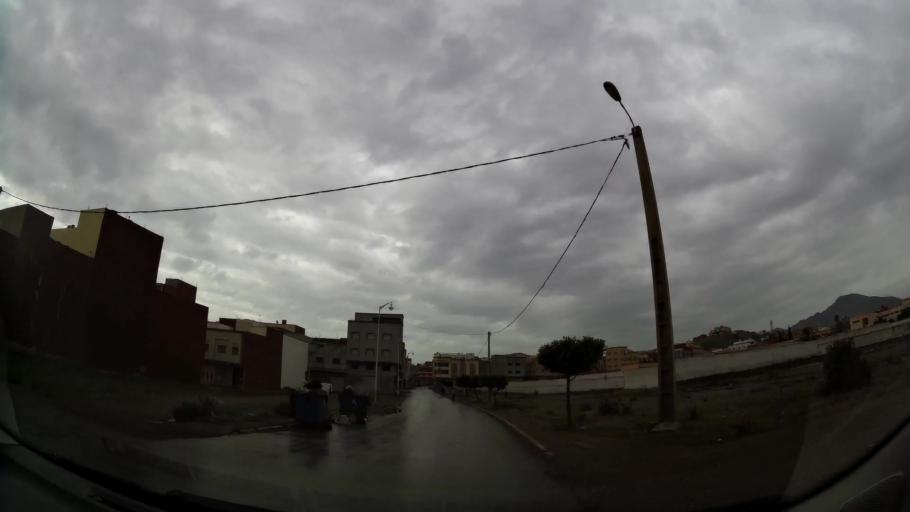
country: MA
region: Oriental
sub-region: Nador
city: Nador
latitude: 35.1525
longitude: -2.9990
